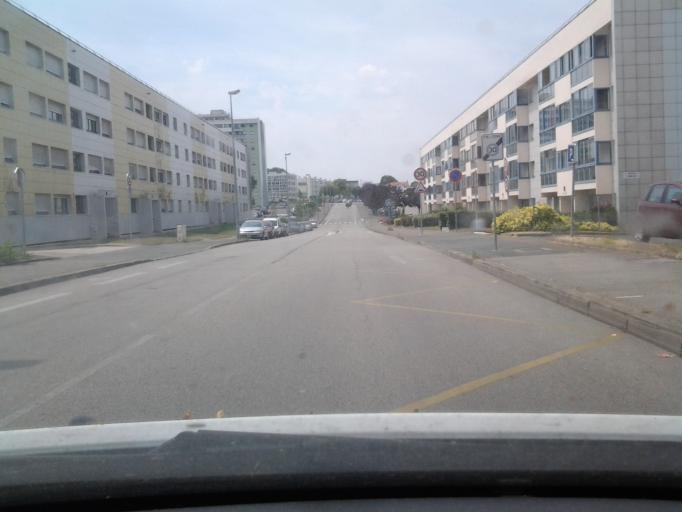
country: FR
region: Pays de la Loire
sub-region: Departement de la Vendee
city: La Roche-sur-Yon
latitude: 46.6804
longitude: -1.4264
